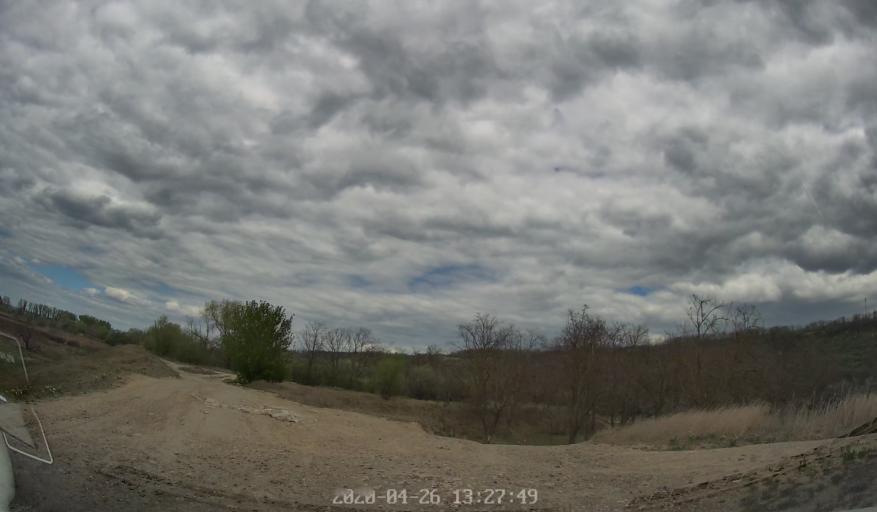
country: MD
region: Criuleni
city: Criuleni
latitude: 47.2053
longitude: 29.1769
